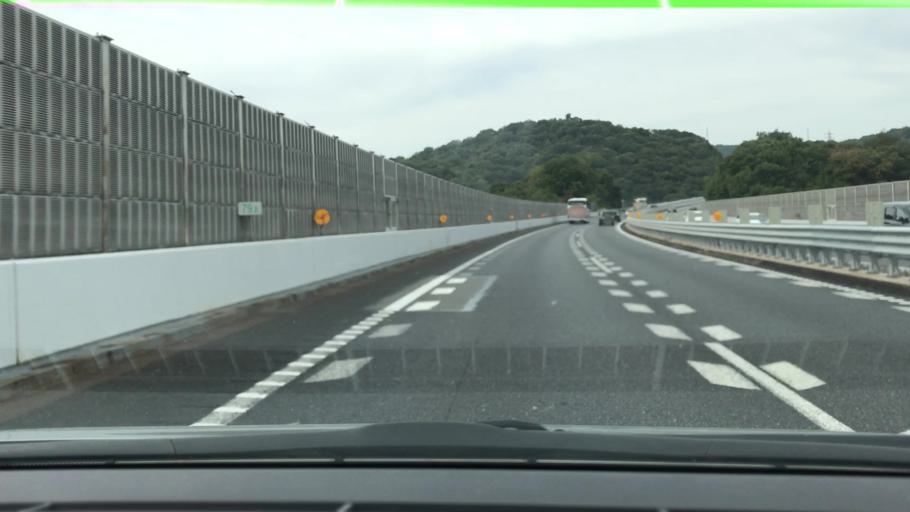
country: JP
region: Hyogo
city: Aioi
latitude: 34.8078
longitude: 134.4514
